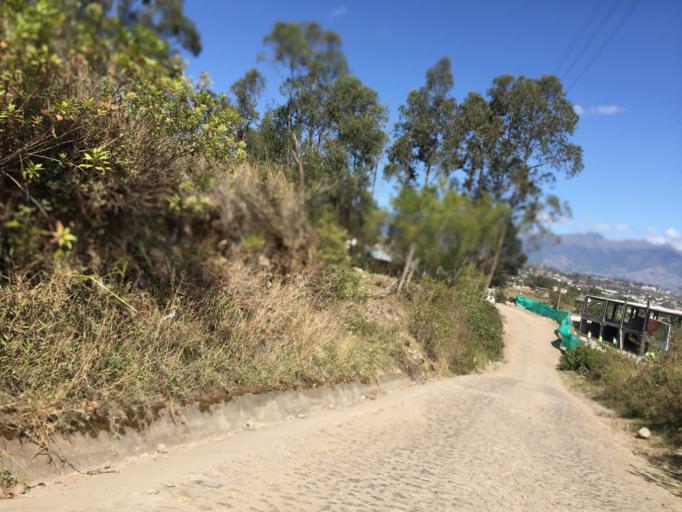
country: EC
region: Imbabura
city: Ibarra
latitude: 0.3093
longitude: -78.1522
